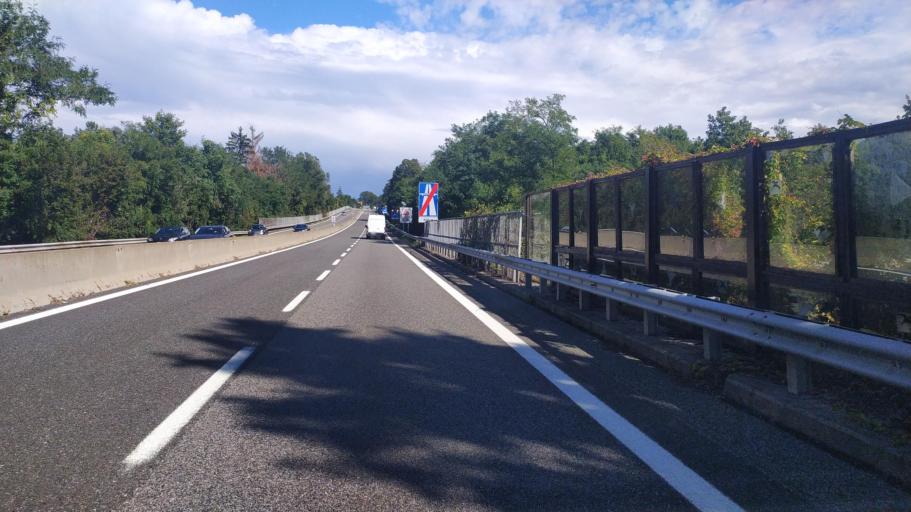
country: IT
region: Lombardy
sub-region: Provincia di Varese
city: Gazzada Schianno
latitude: 45.7861
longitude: 8.8227
